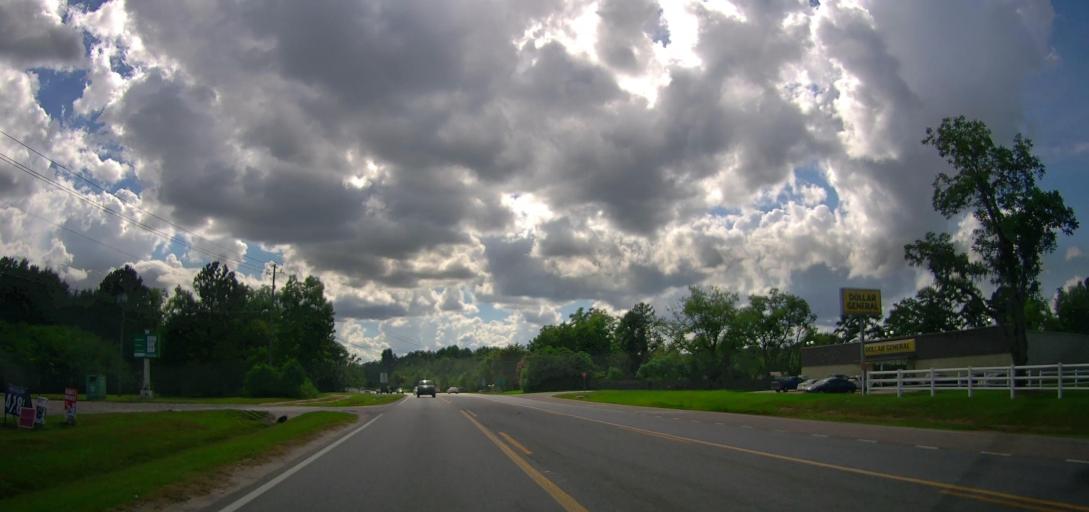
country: US
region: Alabama
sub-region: Russell County
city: Ladonia
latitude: 32.4565
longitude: -85.1933
